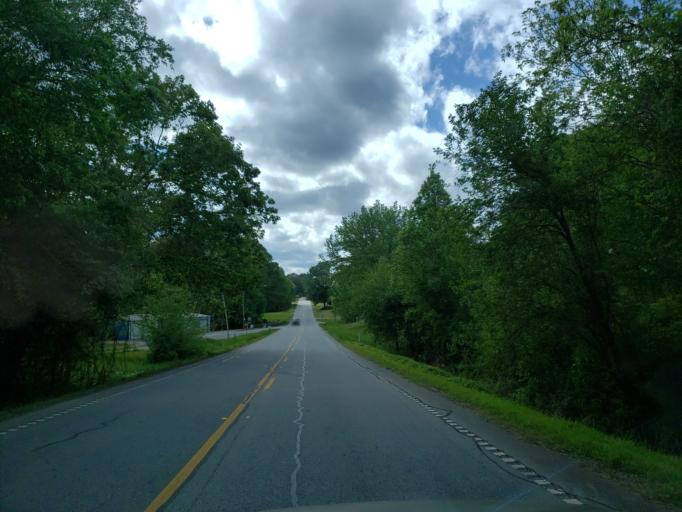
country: US
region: Georgia
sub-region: Haralson County
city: Bremen
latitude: 33.7047
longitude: -85.1874
